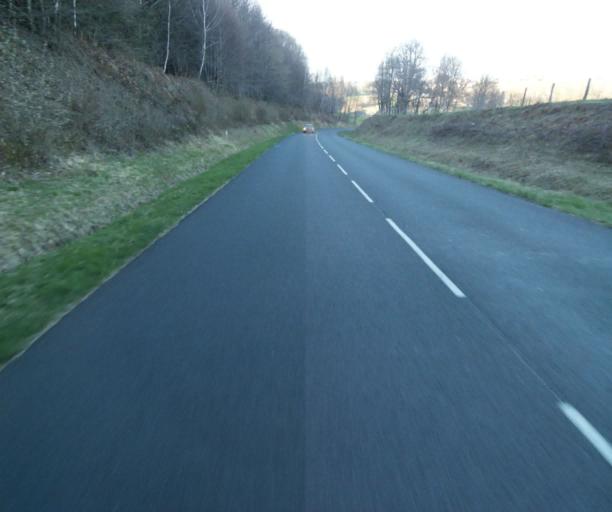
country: FR
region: Limousin
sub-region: Departement de la Correze
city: Seilhac
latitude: 45.3555
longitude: 1.7085
